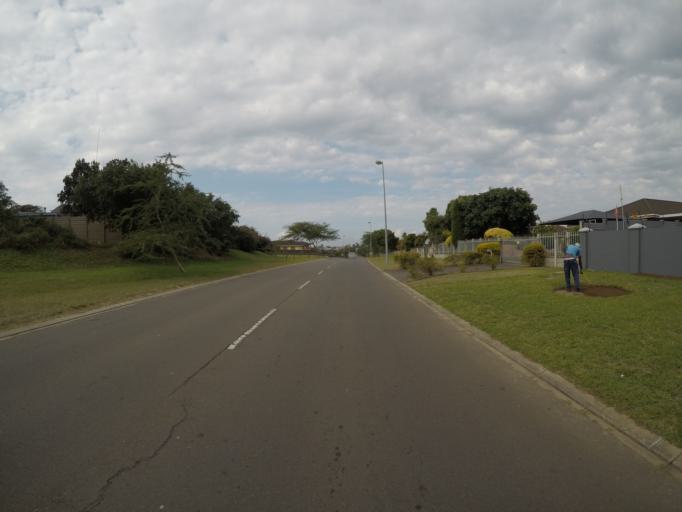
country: ZA
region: KwaZulu-Natal
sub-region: uThungulu District Municipality
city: Richards Bay
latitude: -28.7365
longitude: 32.0887
